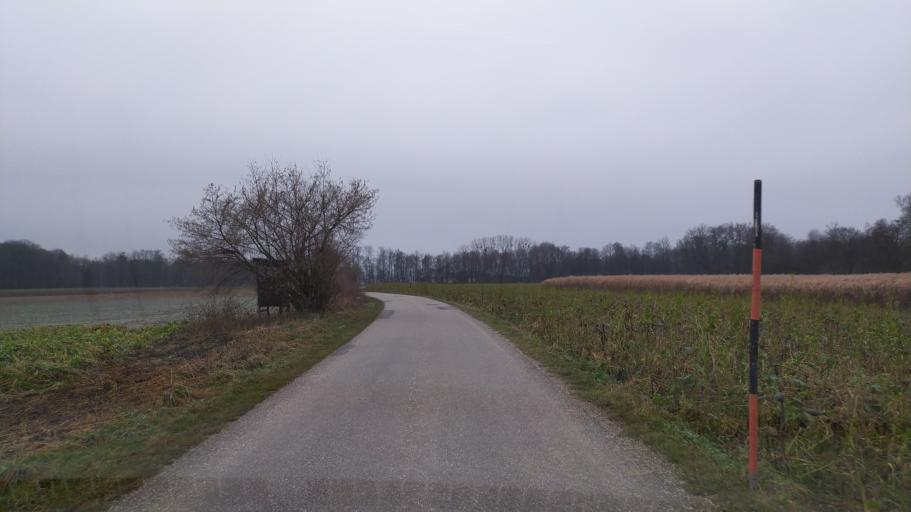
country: AT
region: Upper Austria
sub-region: Politischer Bezirk Perg
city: Perg
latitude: 48.2159
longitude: 14.7203
